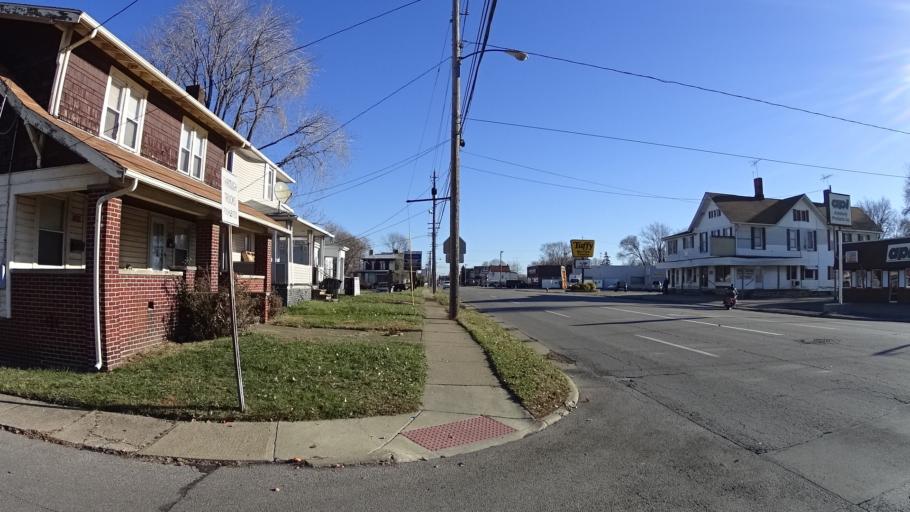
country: US
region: Ohio
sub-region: Lorain County
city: Elyria
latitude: 41.3732
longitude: -82.0928
